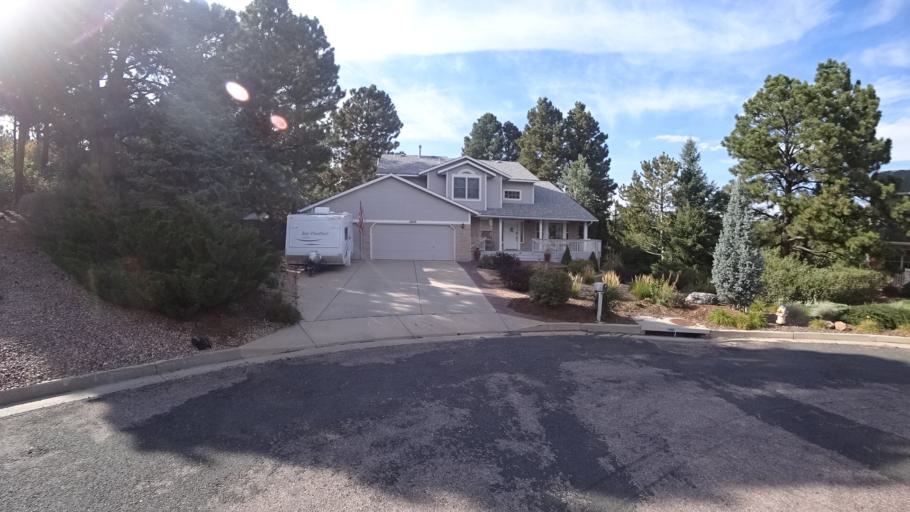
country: US
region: Colorado
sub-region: El Paso County
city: Colorado Springs
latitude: 38.8981
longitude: -104.7782
